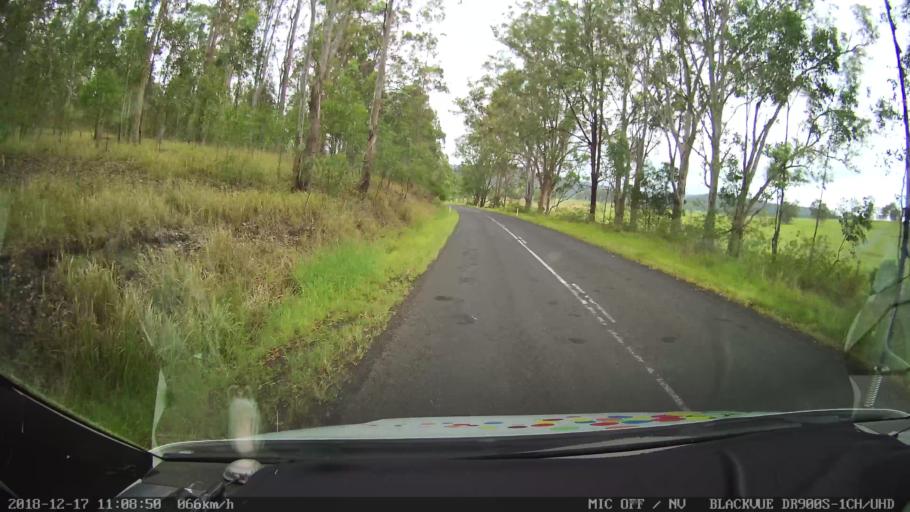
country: AU
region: New South Wales
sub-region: Kyogle
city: Kyogle
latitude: -28.7598
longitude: 152.6553
